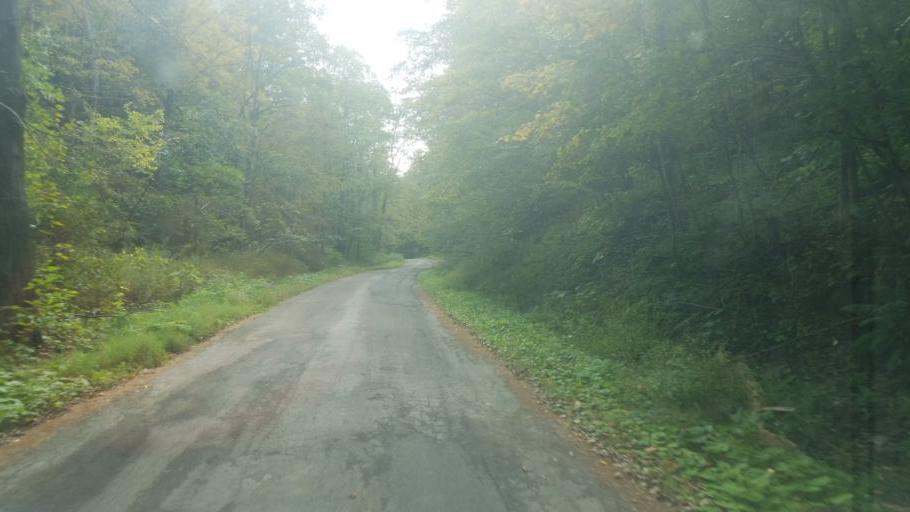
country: US
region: New York
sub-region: Allegany County
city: Cuba
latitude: 42.2205
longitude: -78.3390
